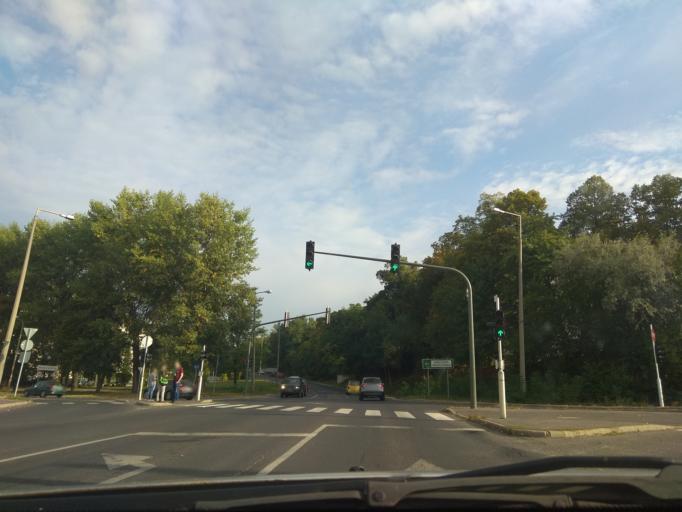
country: HU
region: Borsod-Abauj-Zemplen
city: Miskolc
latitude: 48.0775
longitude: 20.7722
